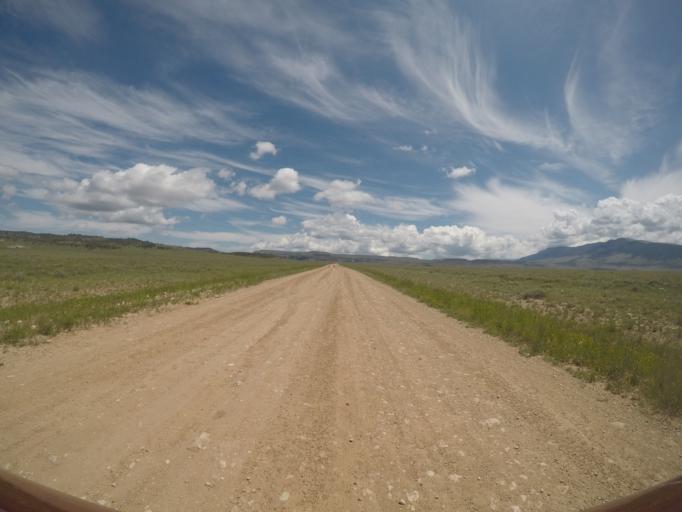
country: US
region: Montana
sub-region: Yellowstone County
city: Laurel
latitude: 45.2325
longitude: -108.6971
